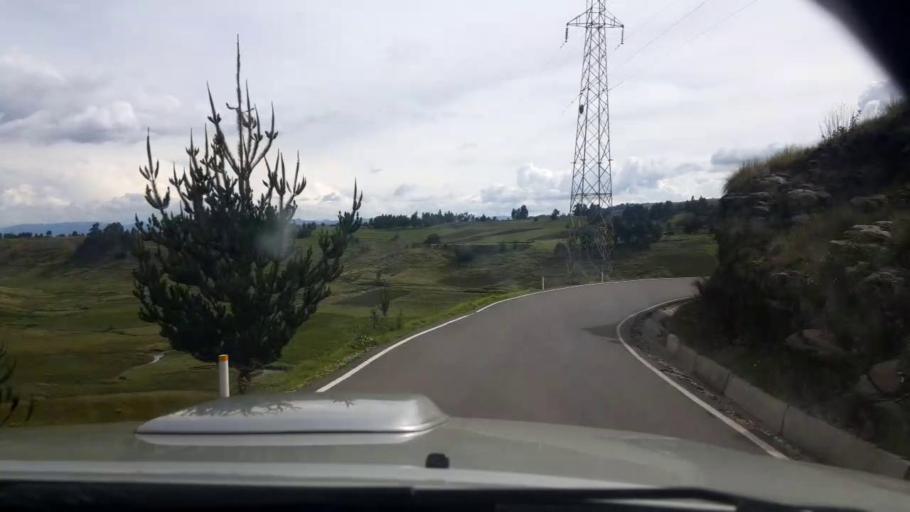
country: PE
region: Ayacucho
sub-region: Provincia de Cangallo
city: Pampa Cangallo
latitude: -13.4506
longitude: -74.1989
